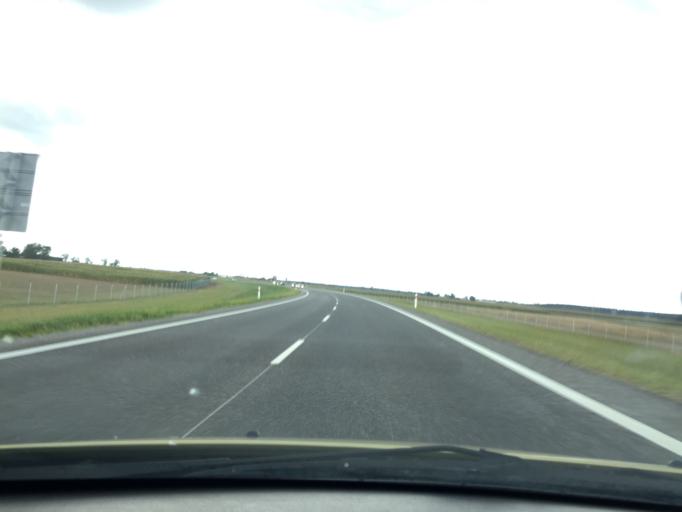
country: PL
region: Greater Poland Voivodeship
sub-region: Powiat sredzki
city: Nowe Miasto nad Warta
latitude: 52.0424
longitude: 17.4599
